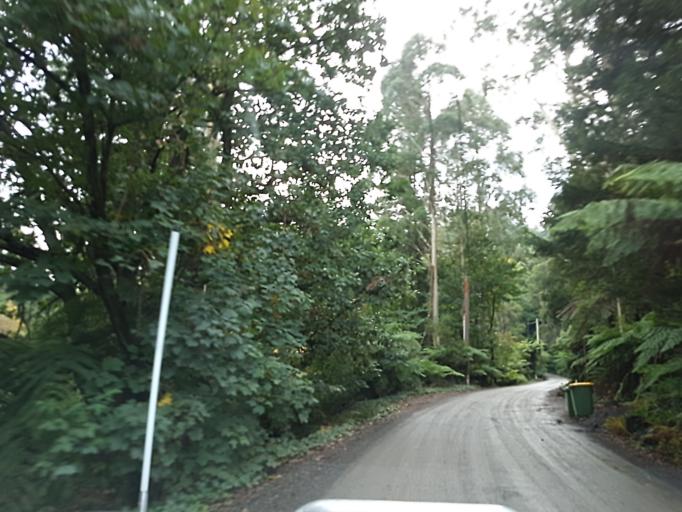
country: AU
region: Victoria
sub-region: Yarra Ranges
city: Monbulk
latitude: -37.8805
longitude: 145.3851
